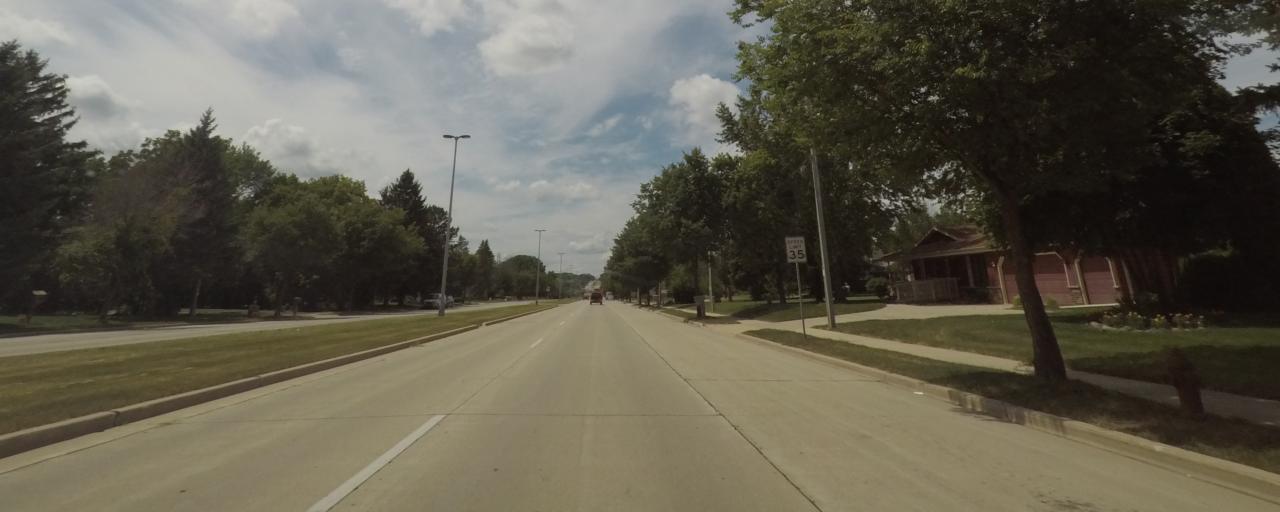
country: US
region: Wisconsin
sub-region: Milwaukee County
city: Greenfield
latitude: 42.9593
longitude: -88.0310
